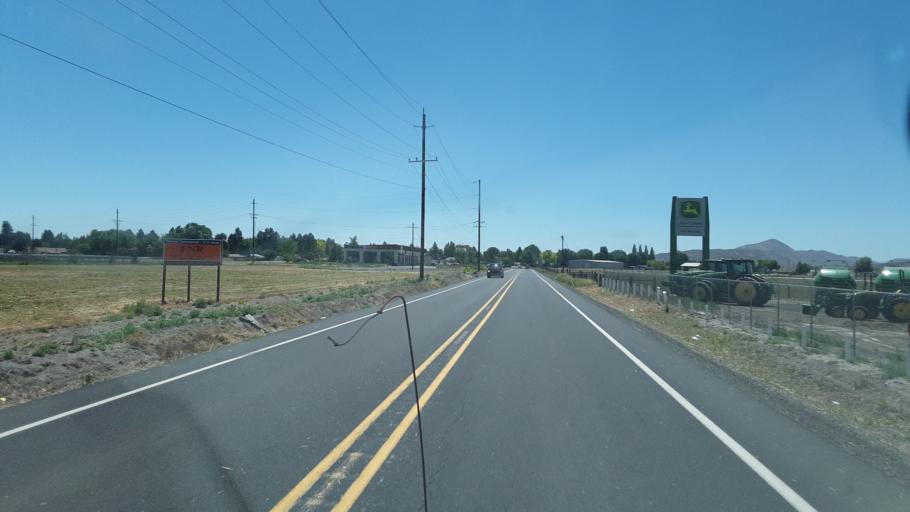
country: US
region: California
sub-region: Siskiyou County
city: Tulelake
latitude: 42.0289
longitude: -121.6123
